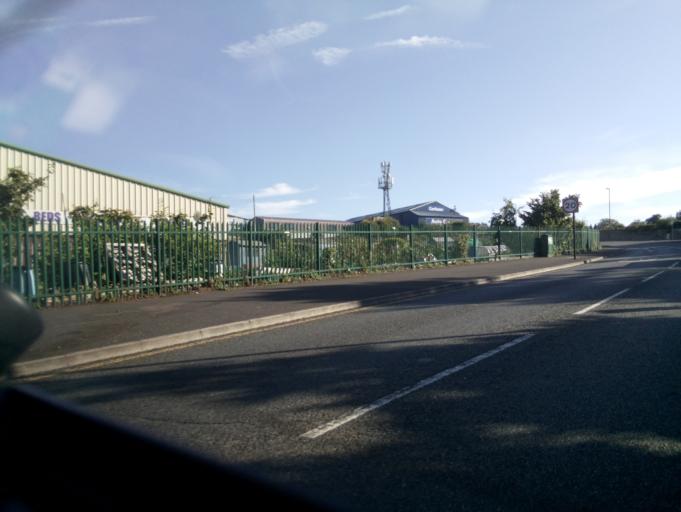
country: GB
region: England
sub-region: South Gloucestershire
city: Kingswood
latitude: 51.4545
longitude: -2.5522
